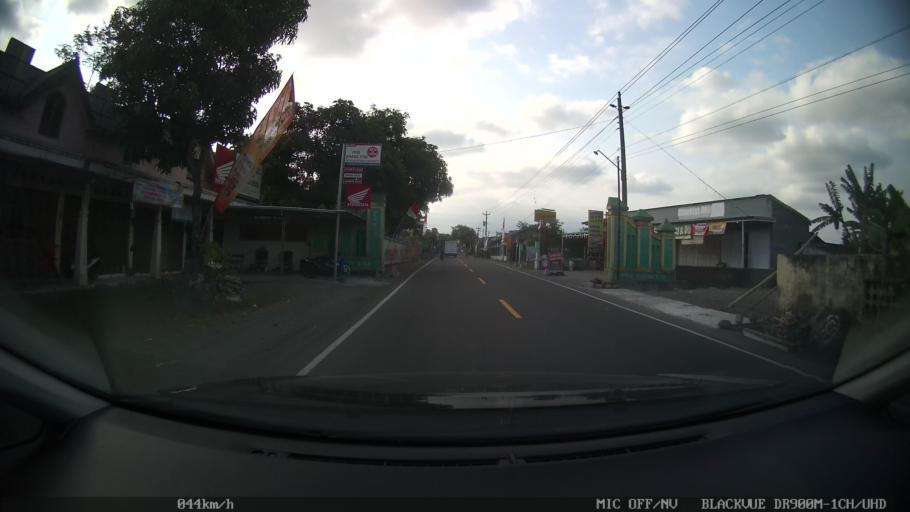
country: ID
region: Central Java
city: Candi Prambanan
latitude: -7.7164
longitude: 110.4723
